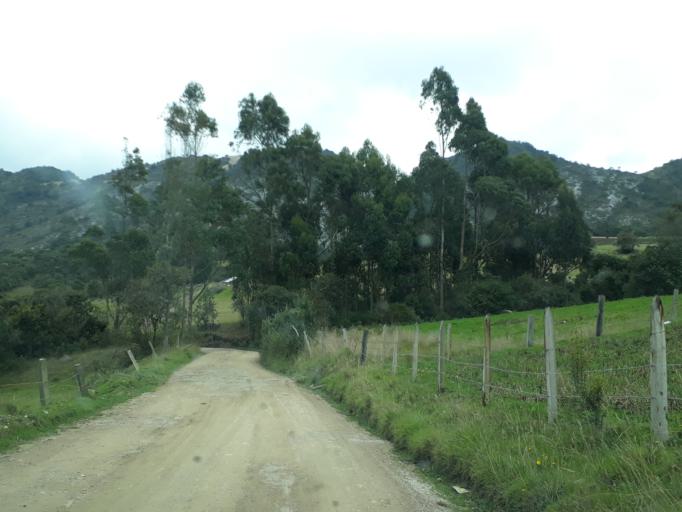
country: CO
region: Cundinamarca
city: Lenguazaque
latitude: 5.3139
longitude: -73.6323
